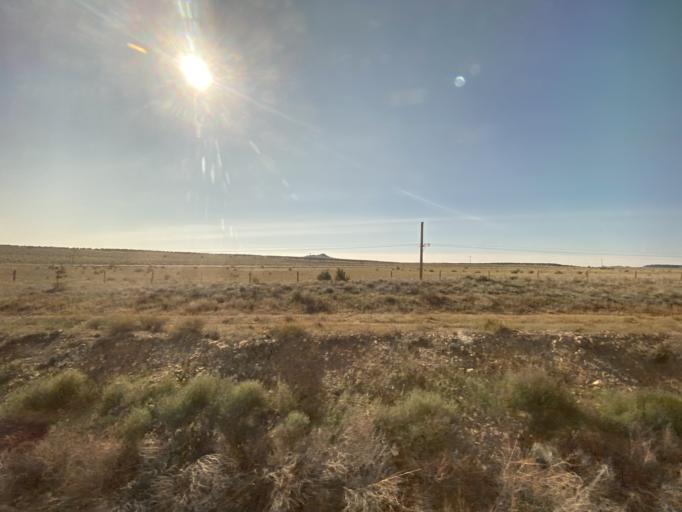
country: US
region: Colorado
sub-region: Otero County
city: Fowler
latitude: 37.5742
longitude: -104.0510
